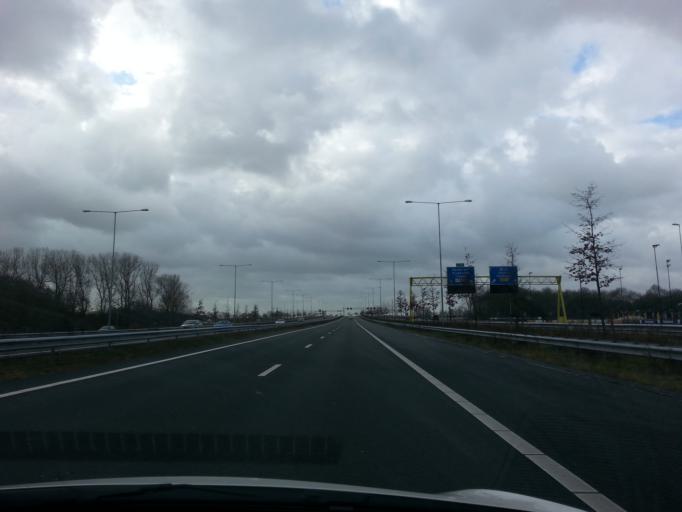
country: NL
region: North Brabant
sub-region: Gemeente 's-Hertogenbosch
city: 's-Hertogenbosch
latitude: 51.6898
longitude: 5.3496
